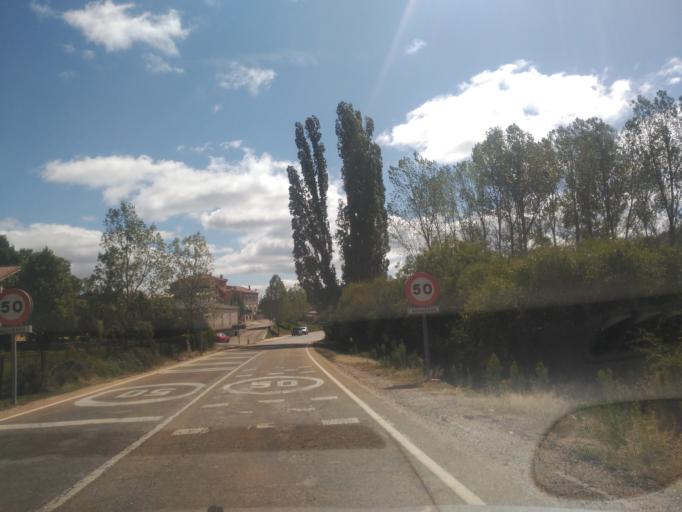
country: ES
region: Castille and Leon
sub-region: Provincia de Soria
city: Casarejos
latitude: 41.7984
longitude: -3.0367
